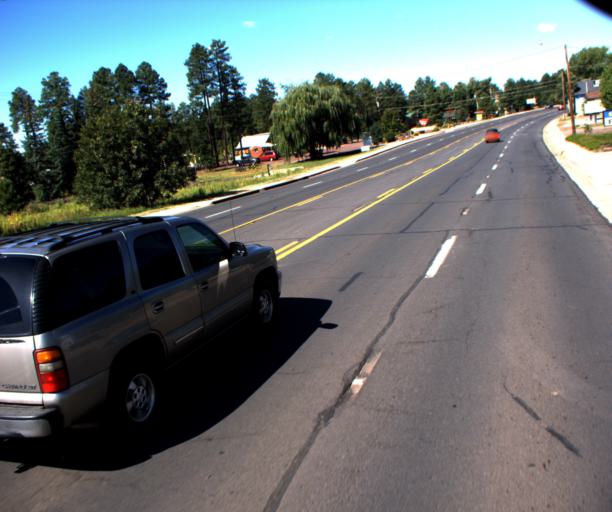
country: US
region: Arizona
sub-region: Navajo County
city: Pinetop-Lakeside
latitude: 34.1259
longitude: -109.9389
